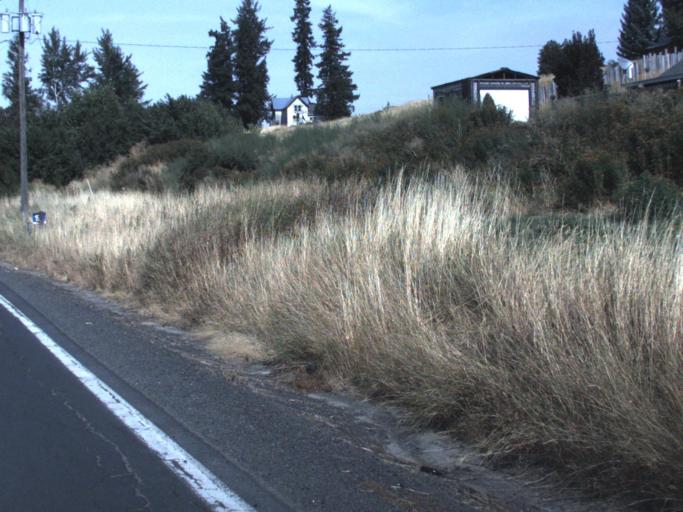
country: US
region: Idaho
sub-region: Benewah County
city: Plummer
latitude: 47.2815
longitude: -117.1598
